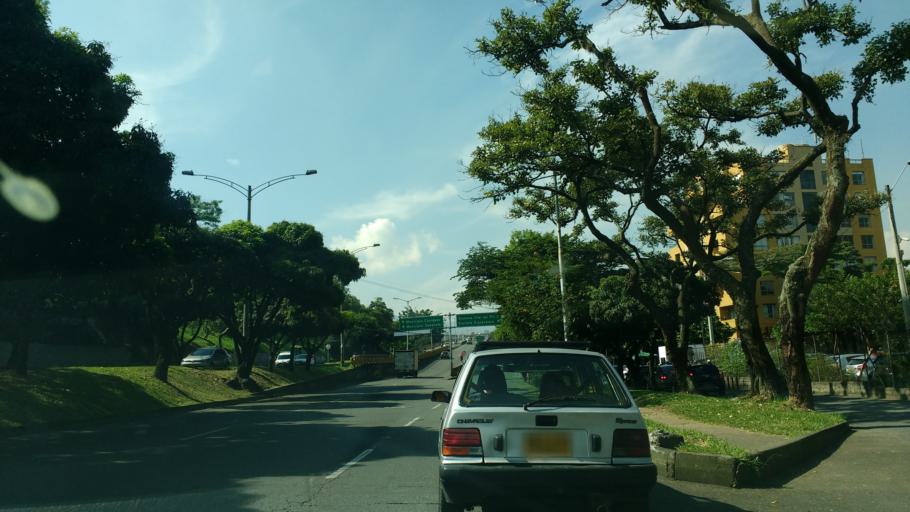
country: CO
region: Antioquia
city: Itagui
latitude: 6.1980
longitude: -75.5782
